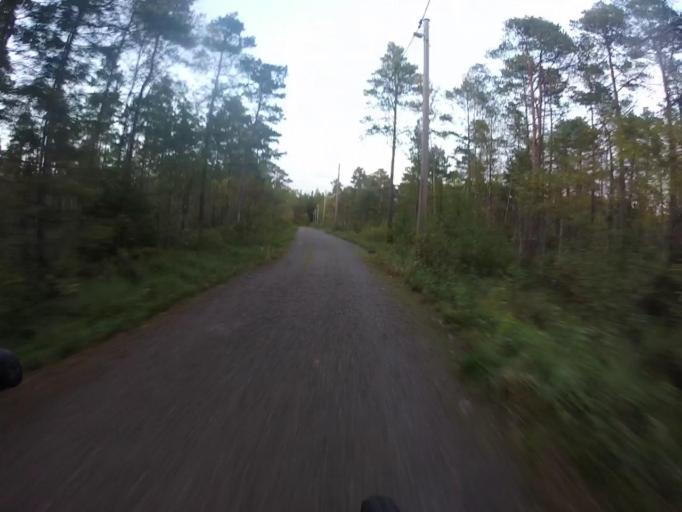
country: SE
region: Vaestra Goetaland
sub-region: Trollhattan
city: Trollhattan
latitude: 58.3003
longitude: 12.2680
